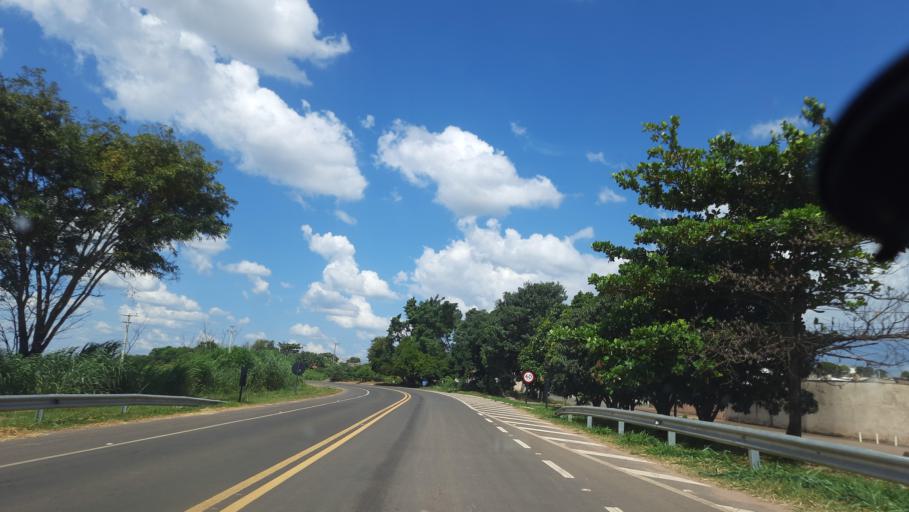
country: BR
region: Sao Paulo
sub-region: Sao Jose Do Rio Pardo
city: Sao Jose do Rio Pardo
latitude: -21.6068
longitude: -46.9360
